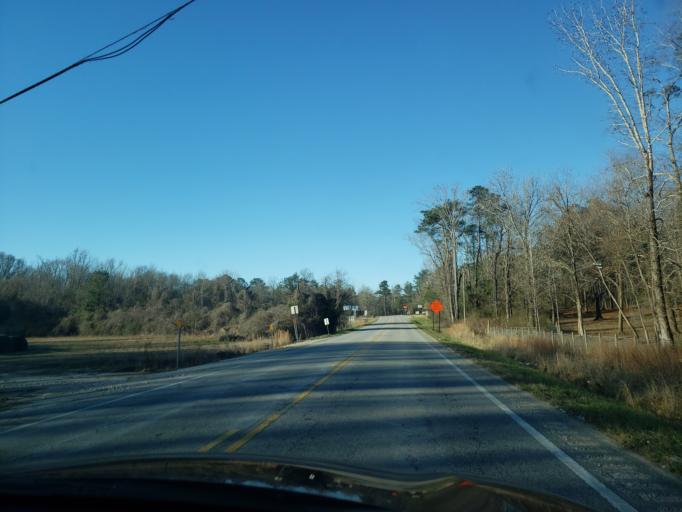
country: US
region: Alabama
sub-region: Macon County
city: Tuskegee
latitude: 32.5727
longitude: -85.6597
